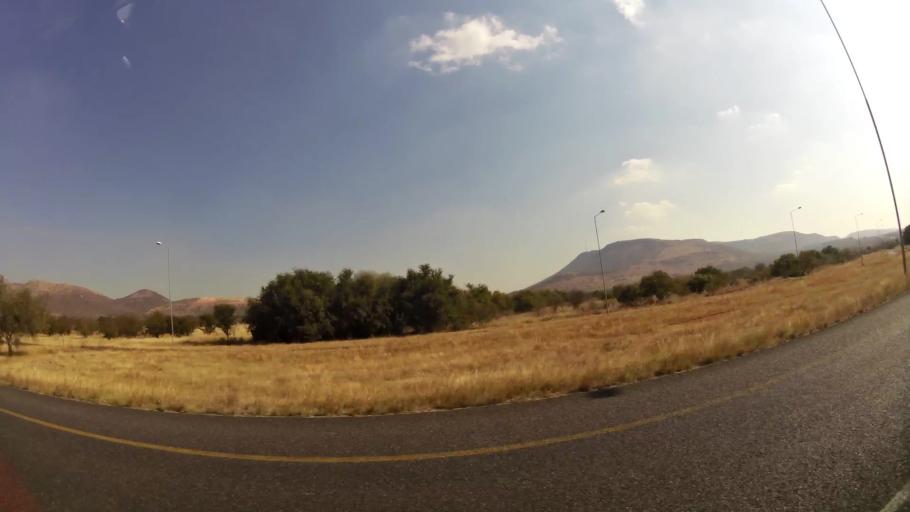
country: ZA
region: North-West
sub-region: Bojanala Platinum District Municipality
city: Rustenburg
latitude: -25.6155
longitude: 27.1541
